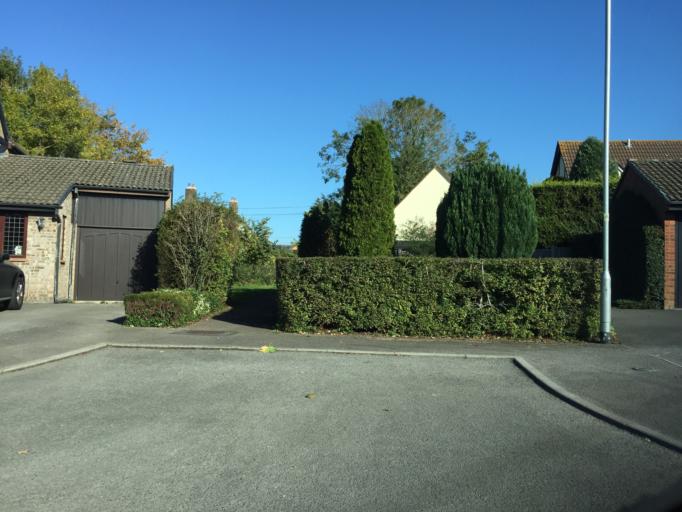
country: GB
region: England
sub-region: South Gloucestershire
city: Yate
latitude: 51.5501
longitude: -2.4153
